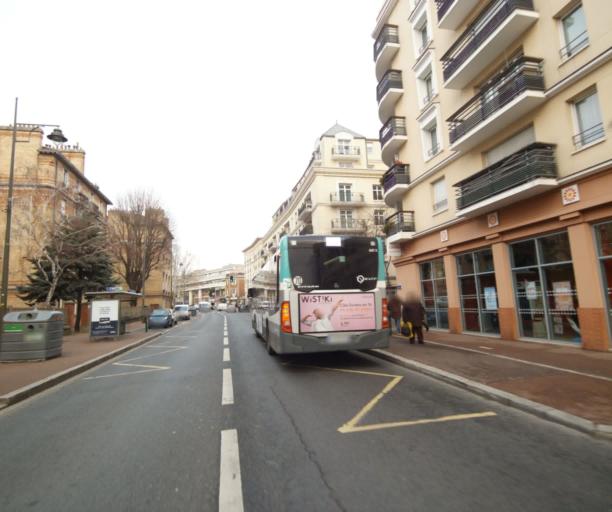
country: FR
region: Ile-de-France
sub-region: Departement des Hauts-de-Seine
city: Saint-Cloud
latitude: 48.8636
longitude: 2.2091
